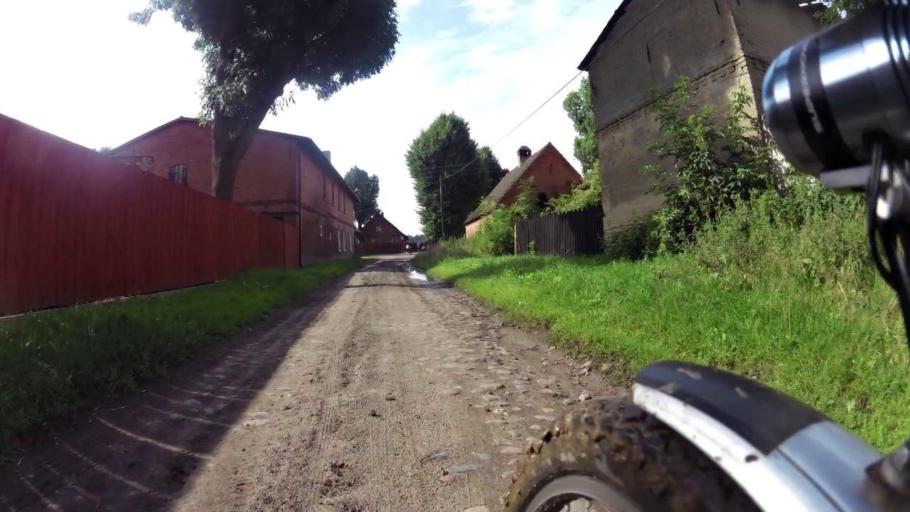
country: PL
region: West Pomeranian Voivodeship
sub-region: Powiat gryfinski
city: Gryfino
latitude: 53.2058
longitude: 14.5779
